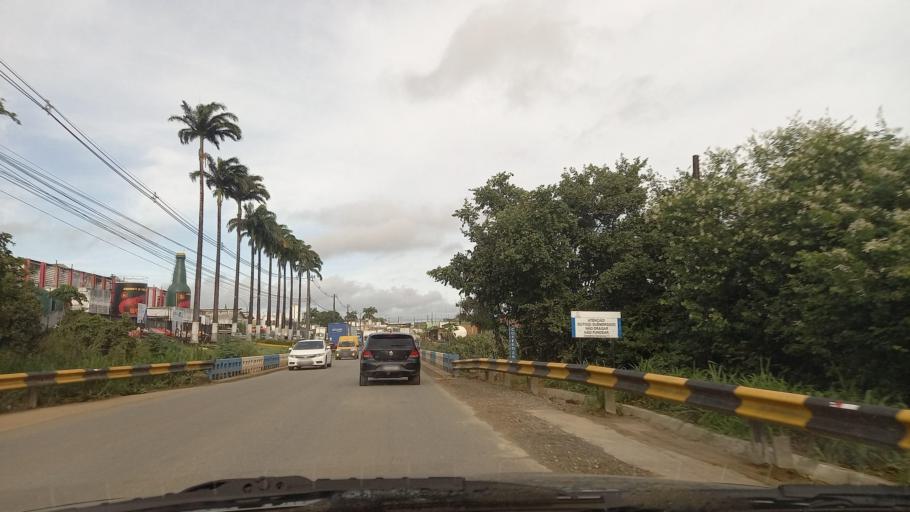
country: BR
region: Pernambuco
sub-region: Vitoria De Santo Antao
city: Vitoria de Santo Antao
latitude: -8.1198
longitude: -35.3207
